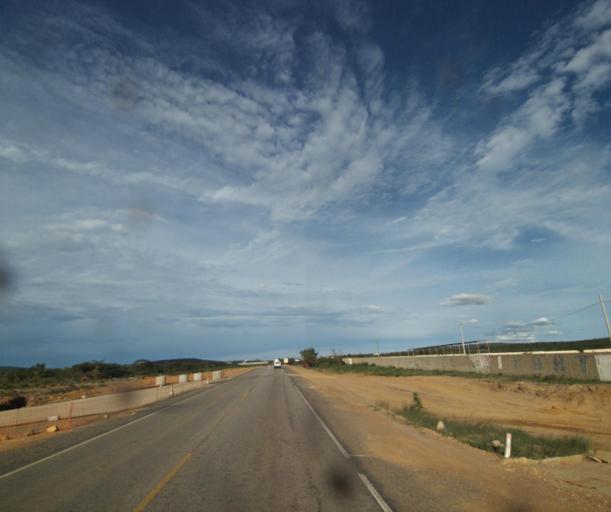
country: BR
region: Bahia
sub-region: Caetite
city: Caetite
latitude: -14.0725
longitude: -42.5403
